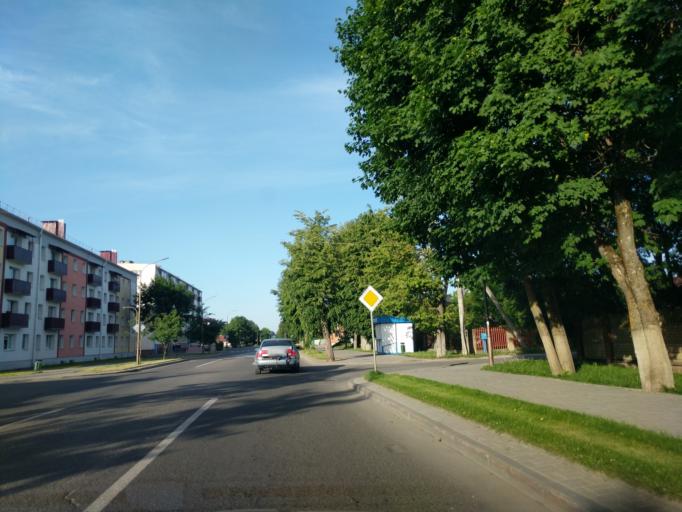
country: BY
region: Grodnenskaya
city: Ashmyany
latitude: 54.4294
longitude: 25.9483
